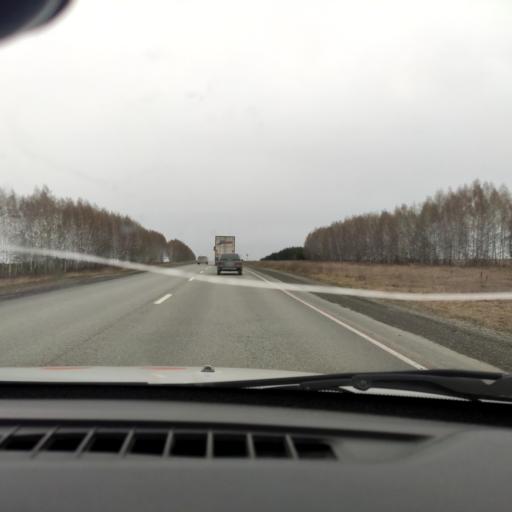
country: RU
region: Bashkortostan
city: Kudeyevskiy
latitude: 54.8092
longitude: 56.6431
